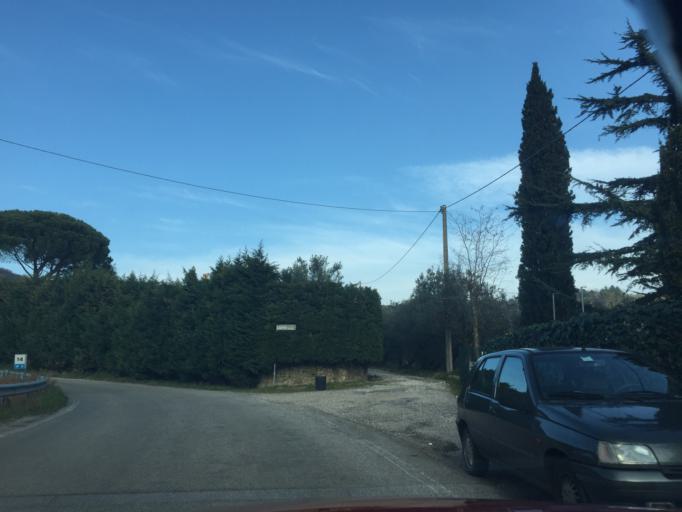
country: IT
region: Tuscany
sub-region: Province of Florence
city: Vinci
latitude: 43.8070
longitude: 10.9298
